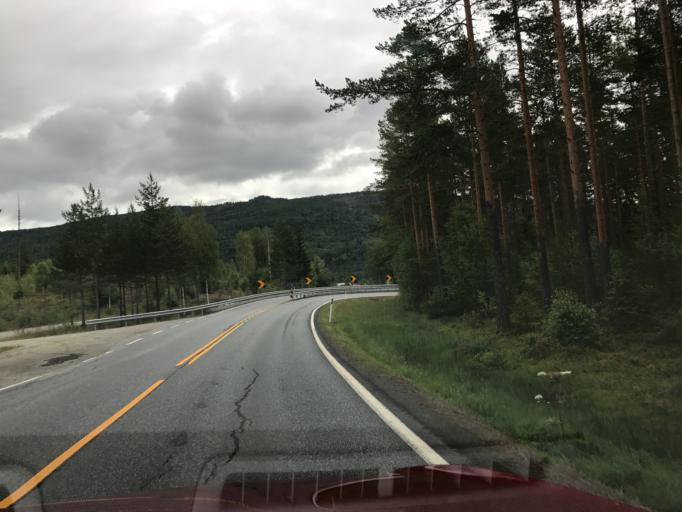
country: NO
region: Buskerud
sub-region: Rollag
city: Rollag
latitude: 60.0131
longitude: 9.2632
